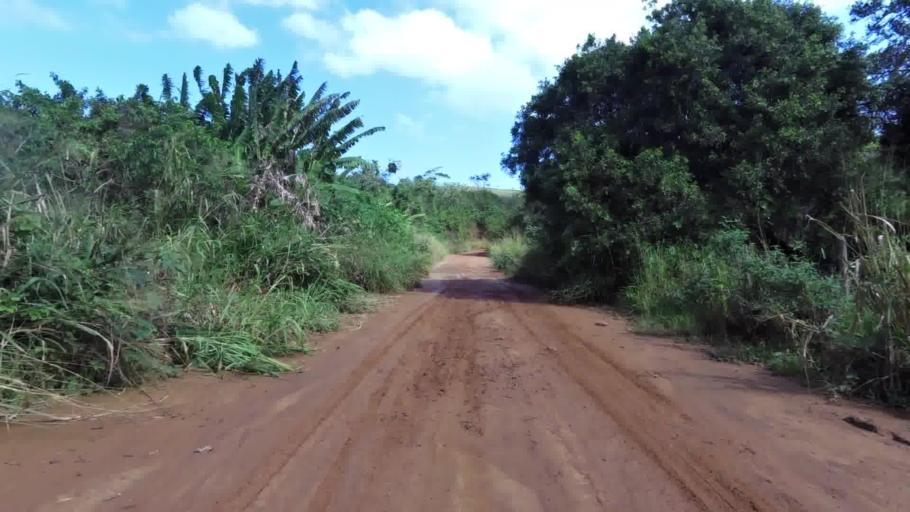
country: BR
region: Espirito Santo
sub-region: Piuma
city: Piuma
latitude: -20.8179
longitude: -40.6767
